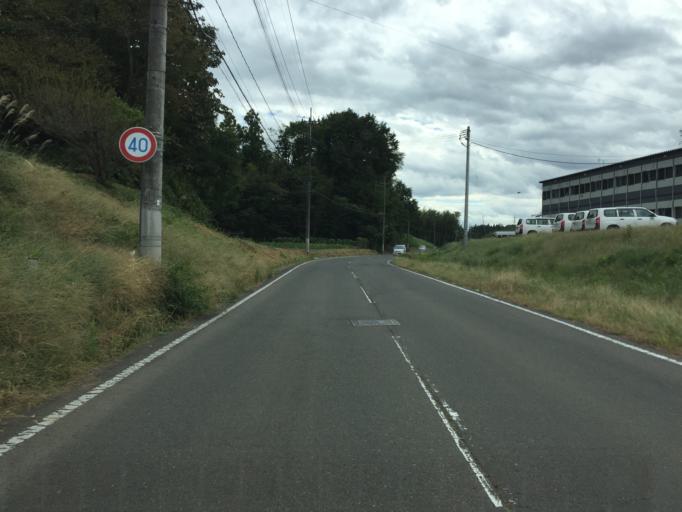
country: JP
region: Fukushima
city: Fukushima-shi
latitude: 37.6970
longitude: 140.4899
